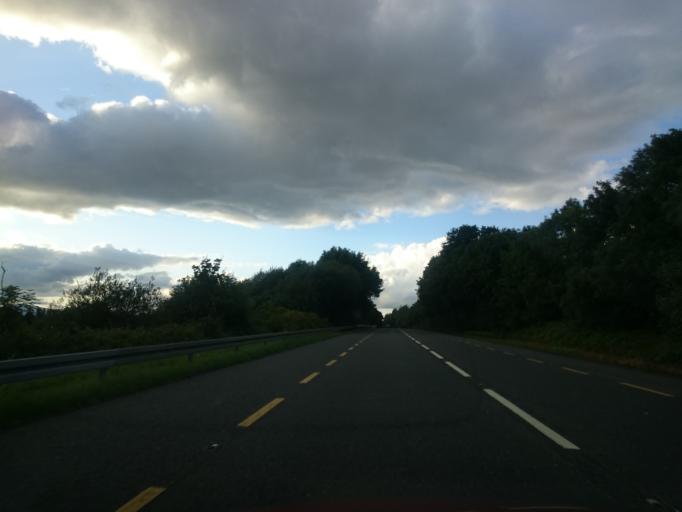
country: IE
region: Leinster
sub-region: Loch Garman
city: Enniscorthy
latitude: 52.4823
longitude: -6.5646
